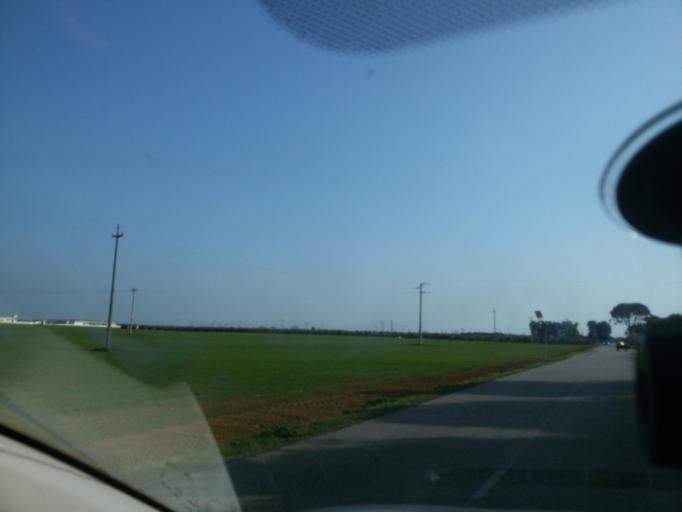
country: IT
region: Apulia
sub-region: Provincia di Brindisi
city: Mesagne
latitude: 40.5944
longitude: 17.8153
